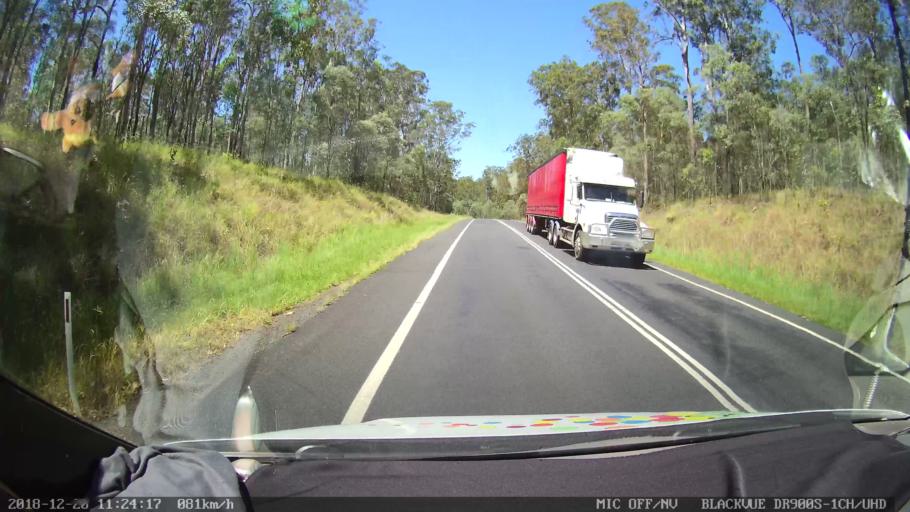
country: AU
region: New South Wales
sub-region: Richmond Valley
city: Casino
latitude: -29.0723
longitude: 153.0029
